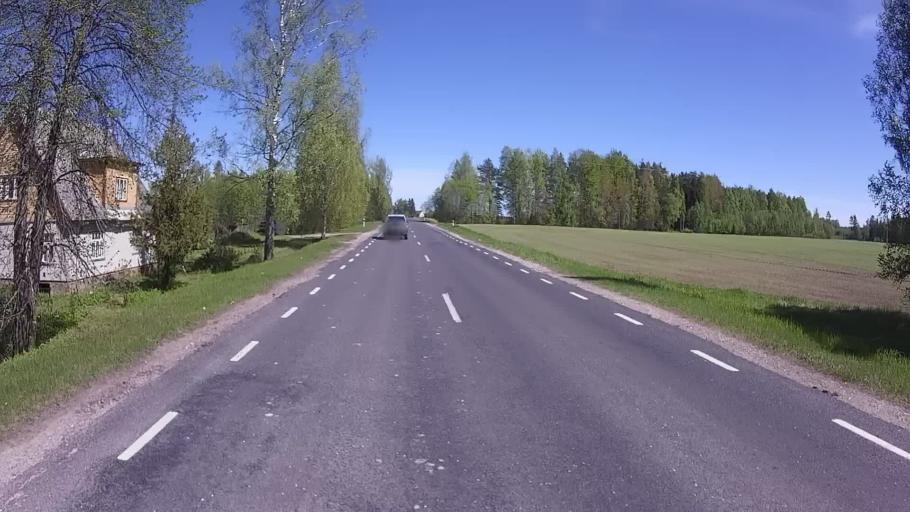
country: EE
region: Polvamaa
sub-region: Raepina vald
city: Rapina
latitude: 58.0295
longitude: 27.3843
